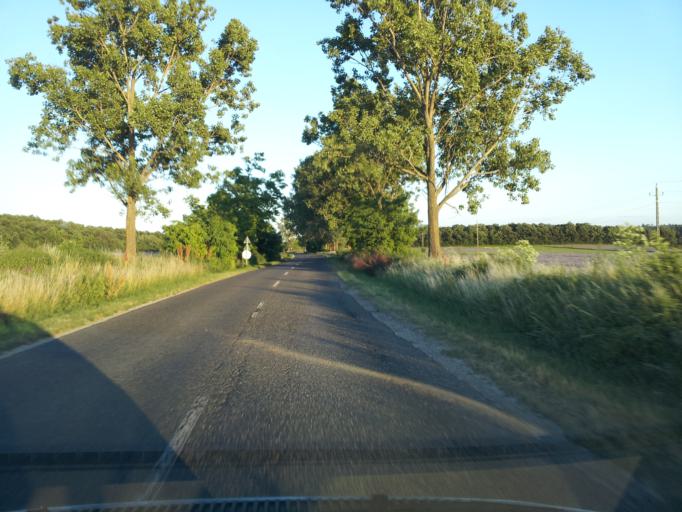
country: HU
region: Veszprem
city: Szentkiralyszabadja
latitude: 47.0318
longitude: 17.9345
